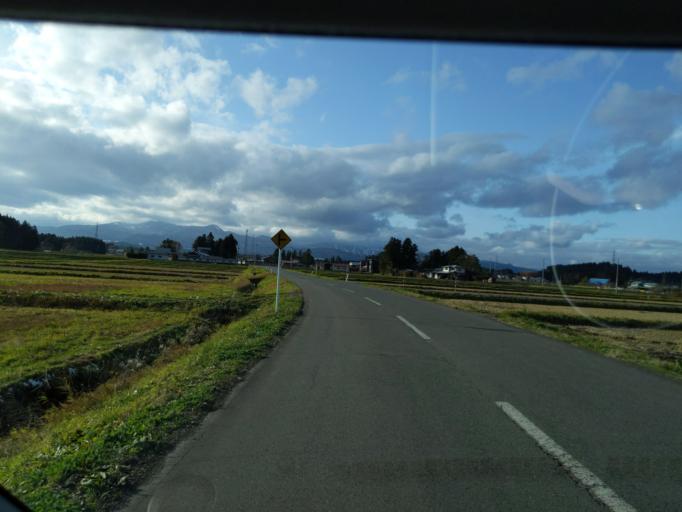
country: JP
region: Iwate
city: Mizusawa
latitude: 39.1898
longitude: 141.0926
